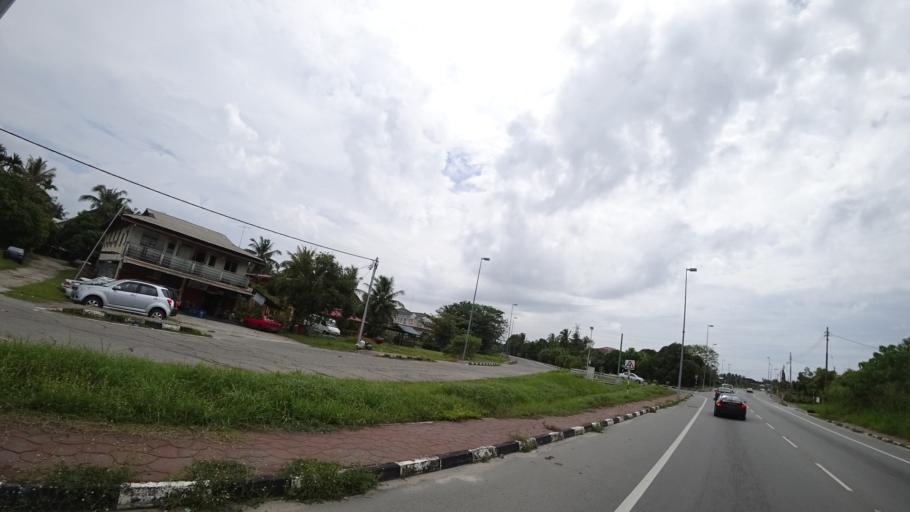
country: BN
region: Tutong
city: Tutong
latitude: 4.8027
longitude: 114.6513
